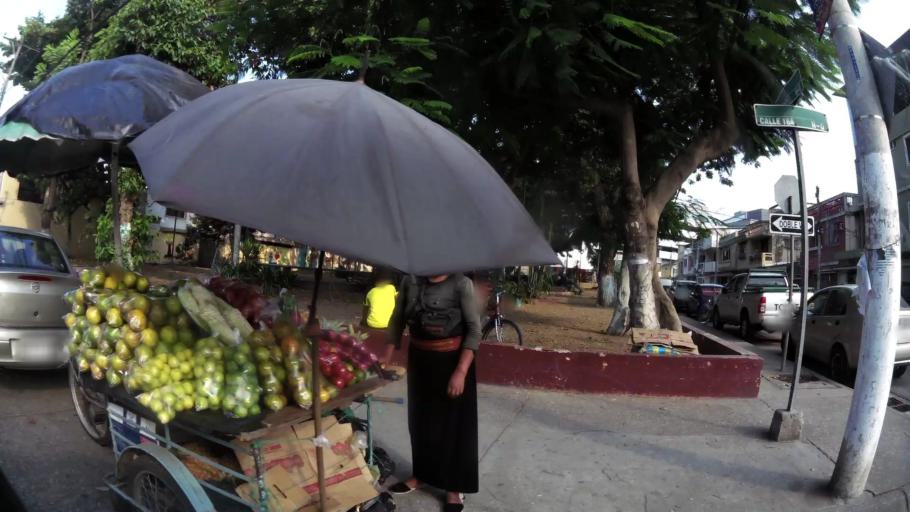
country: EC
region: Guayas
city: Guayaquil
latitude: -2.1493
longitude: -79.9070
